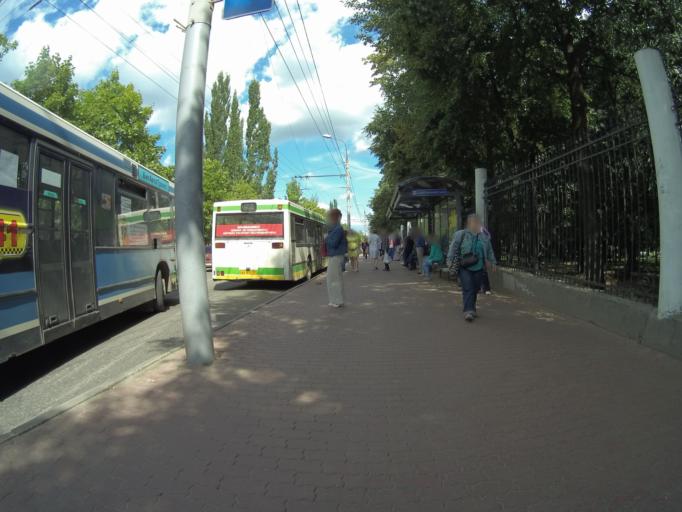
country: RU
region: Vladimir
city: Vladimir
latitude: 56.1411
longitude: 40.4067
